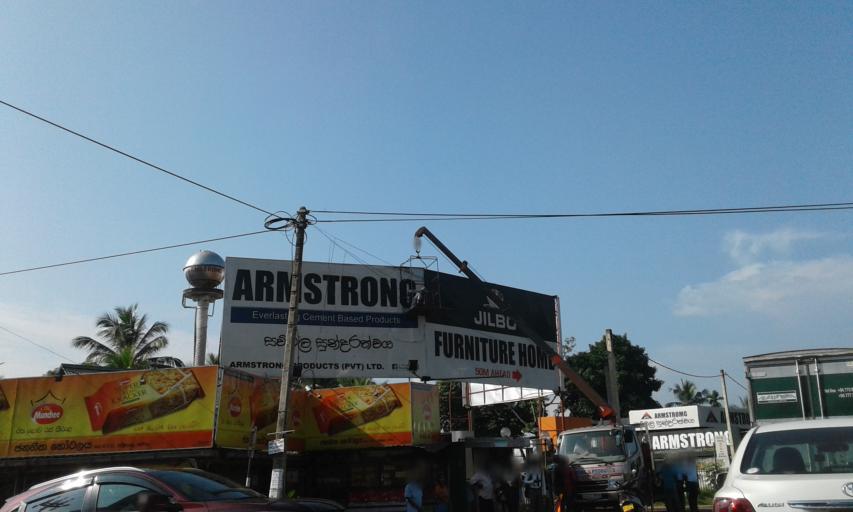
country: LK
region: Western
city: Welisara
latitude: 7.0147
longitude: 79.9690
